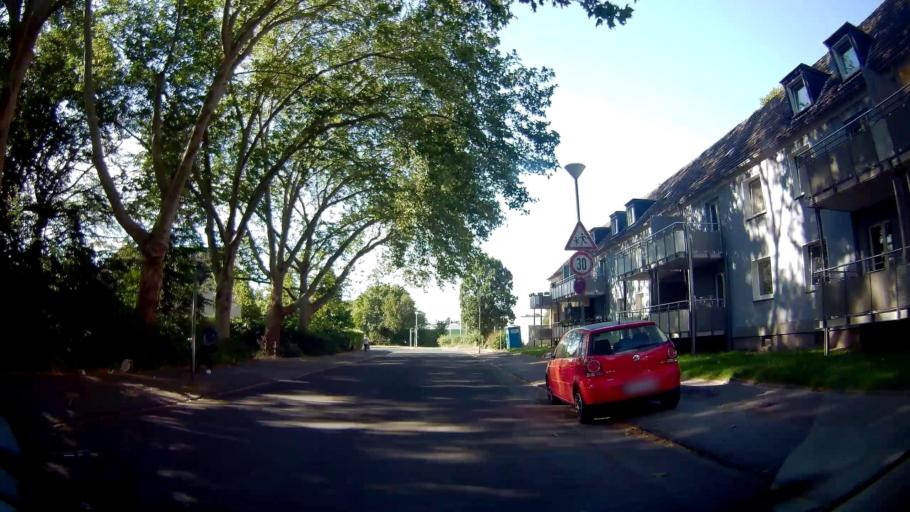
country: DE
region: North Rhine-Westphalia
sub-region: Regierungsbezirk Dusseldorf
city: Essen
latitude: 51.4711
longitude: 6.9983
